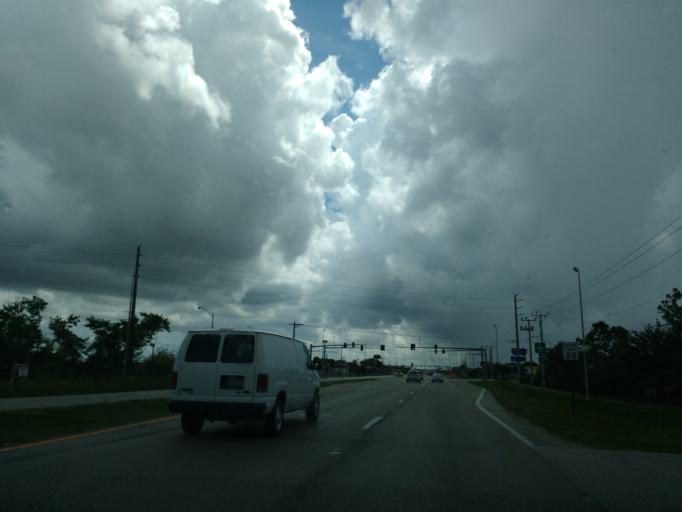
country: US
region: Florida
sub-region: Charlotte County
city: Charlotte Park
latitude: 26.8949
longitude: -82.0125
